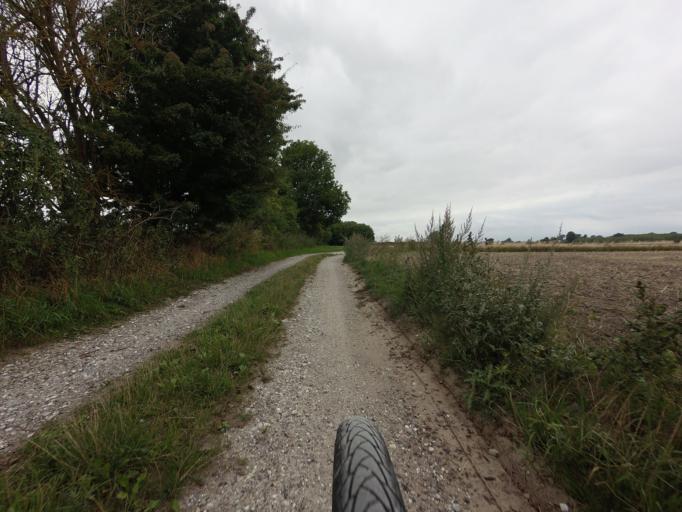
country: DK
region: Zealand
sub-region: Stevns Kommune
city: Store Heddinge
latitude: 55.3315
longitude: 12.4448
